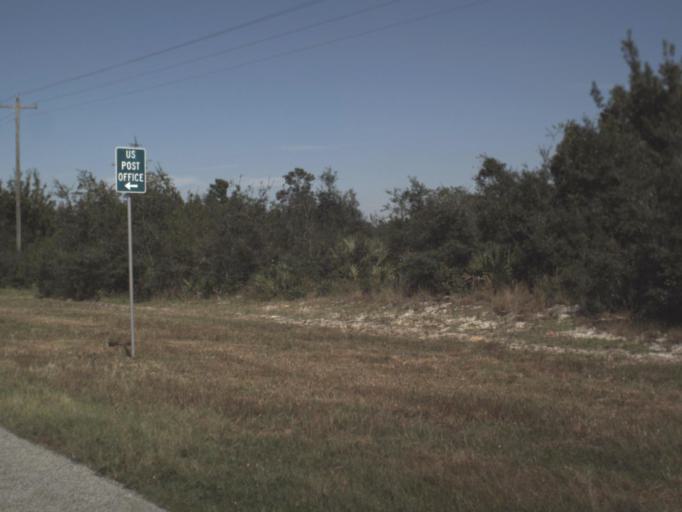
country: US
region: Florida
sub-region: Highlands County
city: Placid Lakes
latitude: 27.1334
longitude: -81.3293
